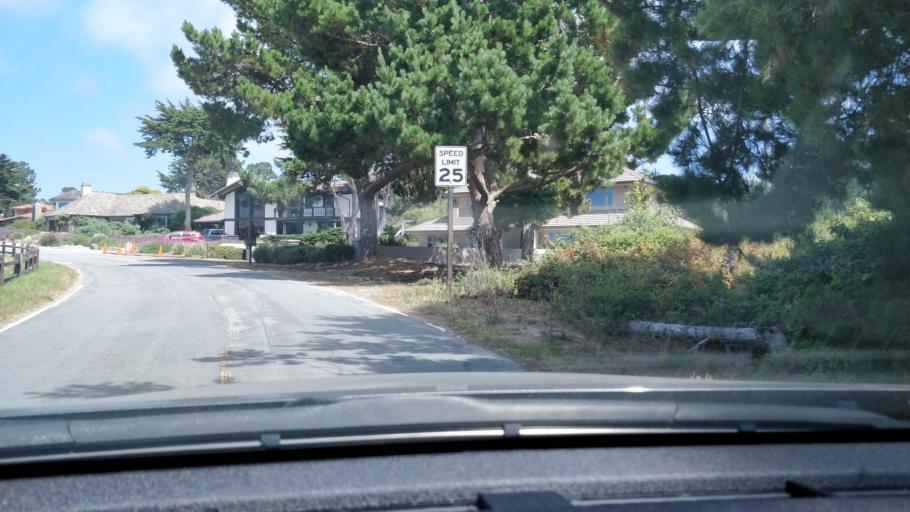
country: US
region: California
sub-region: Monterey County
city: Del Monte Forest
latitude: 36.5903
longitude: -121.9596
